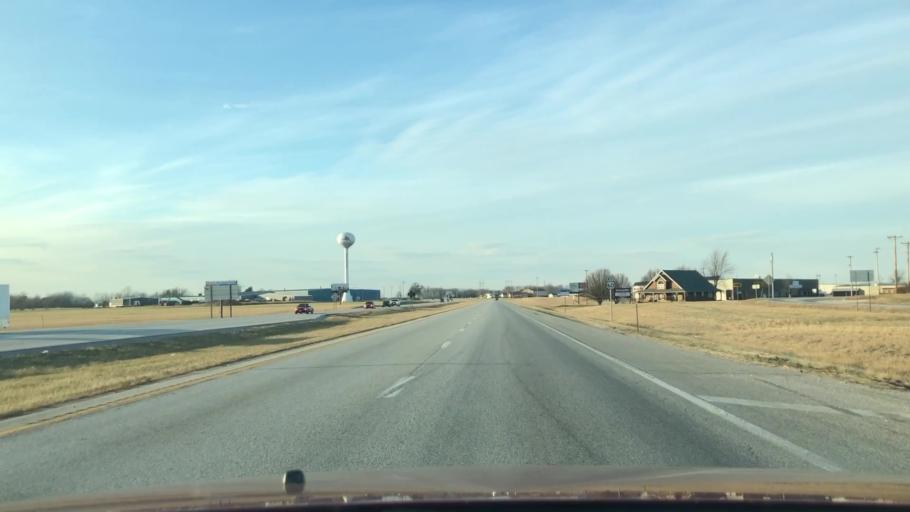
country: US
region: Missouri
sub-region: Webster County
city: Seymour
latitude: 37.1502
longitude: -92.7535
